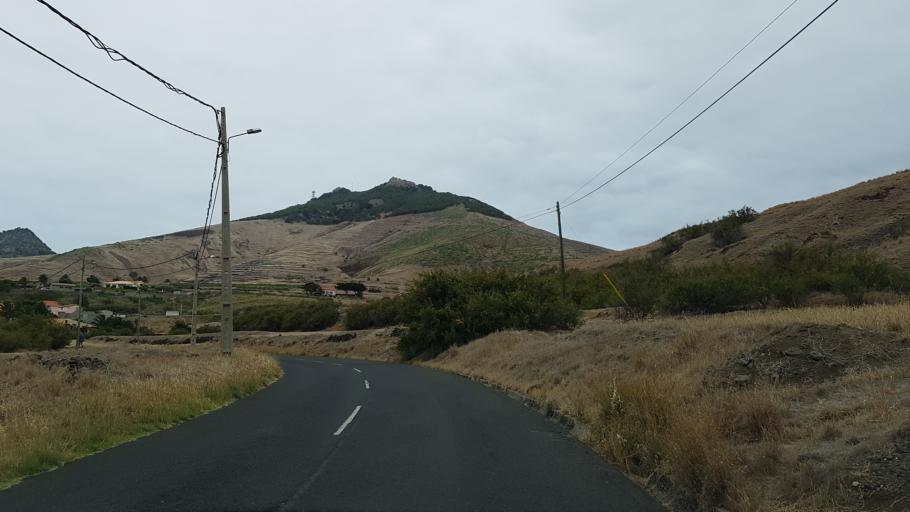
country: PT
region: Madeira
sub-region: Porto Santo
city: Vila de Porto Santo
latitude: 33.0731
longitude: -16.3088
